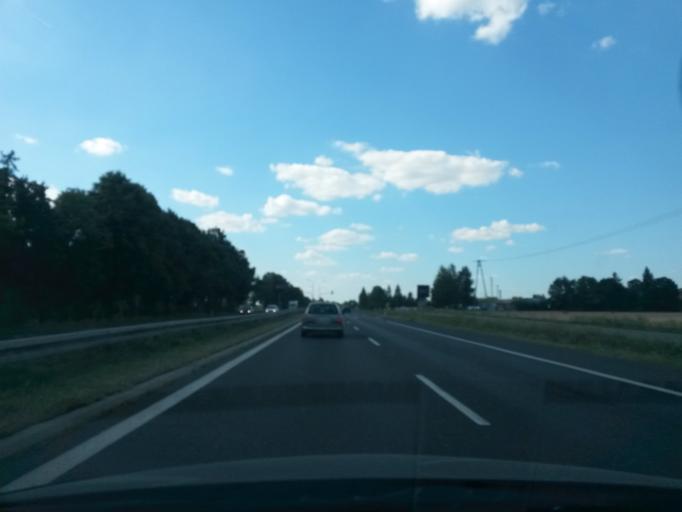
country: PL
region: Masovian Voivodeship
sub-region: Powiat plonski
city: Zaluski
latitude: 52.4803
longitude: 20.5589
